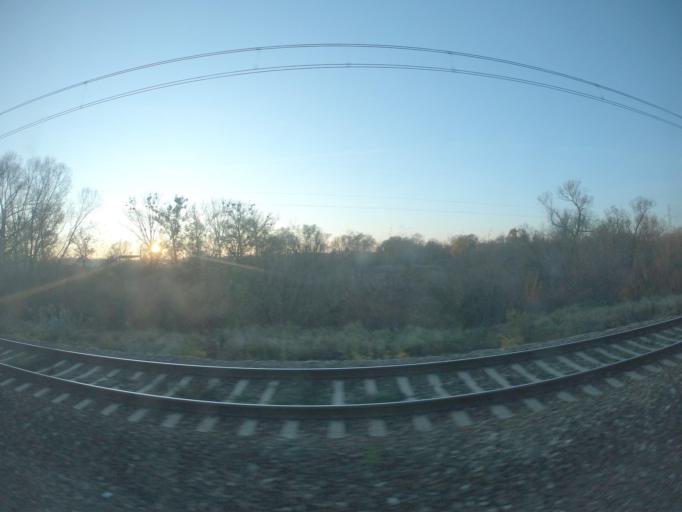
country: PL
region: Lubusz
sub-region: Powiat gorzowski
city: Kostrzyn nad Odra
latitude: 52.5760
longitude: 14.6438
